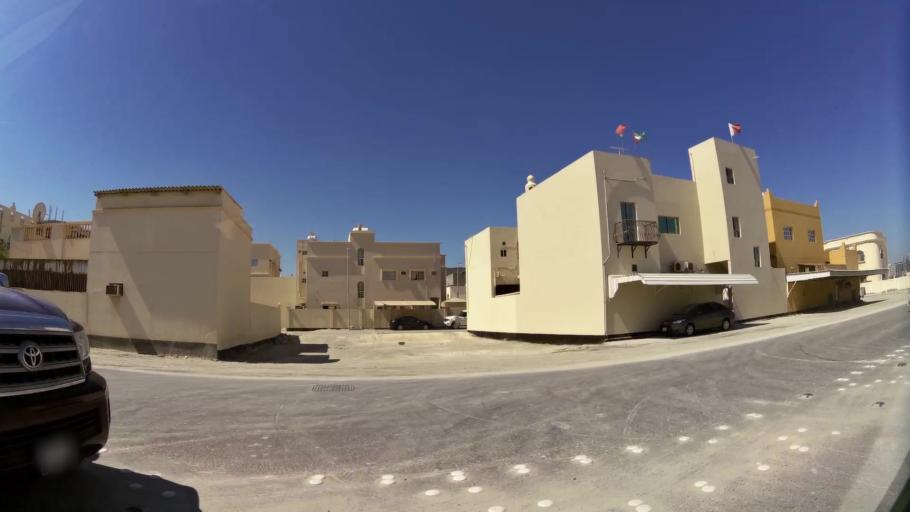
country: BH
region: Muharraq
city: Al Hadd
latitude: 26.2744
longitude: 50.6580
